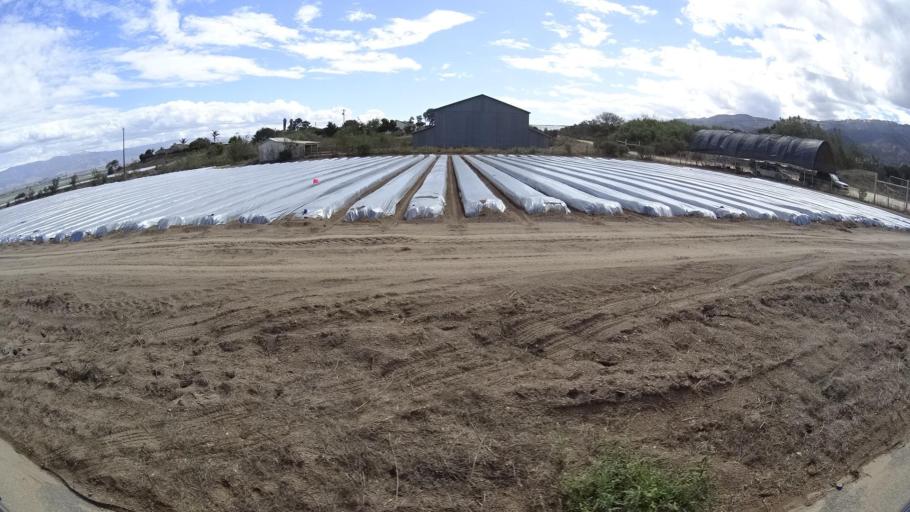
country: US
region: California
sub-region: Monterey County
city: Chualar
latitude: 36.5880
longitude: -121.6068
